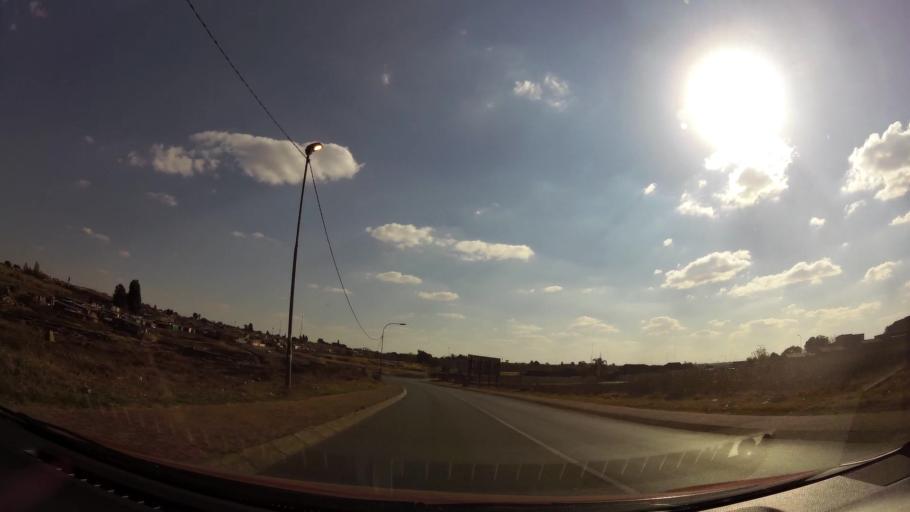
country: ZA
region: Gauteng
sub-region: City of Johannesburg Metropolitan Municipality
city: Soweto
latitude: -26.2244
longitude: 27.8825
